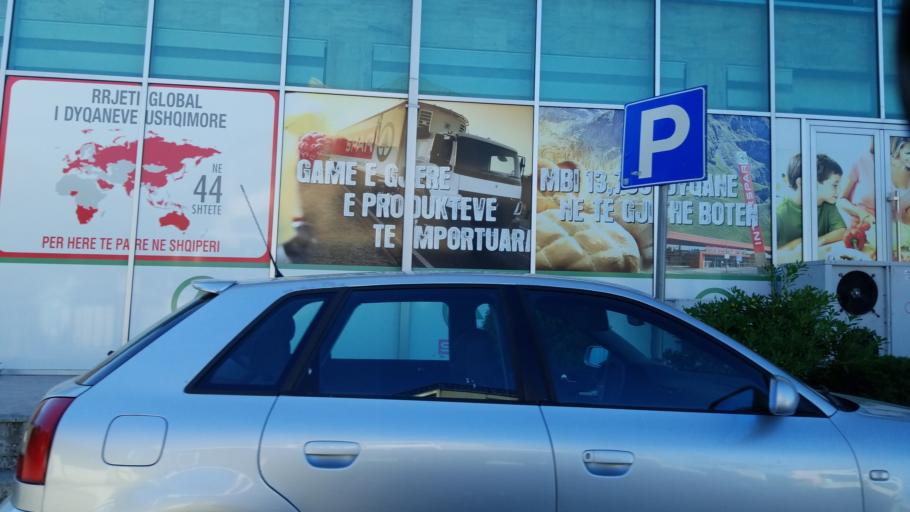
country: AL
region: Shkoder
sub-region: Rrethi i Shkodres
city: Shkoder
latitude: 42.0714
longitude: 19.5067
